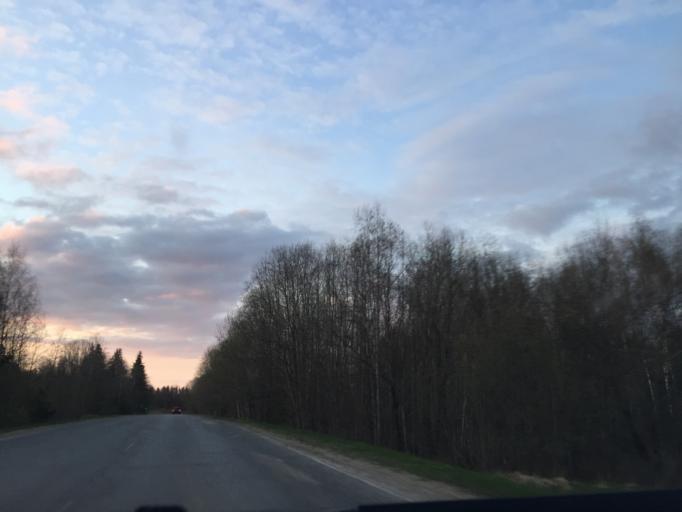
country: LV
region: Aluksnes Rajons
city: Aluksne
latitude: 57.3954
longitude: 27.0466
